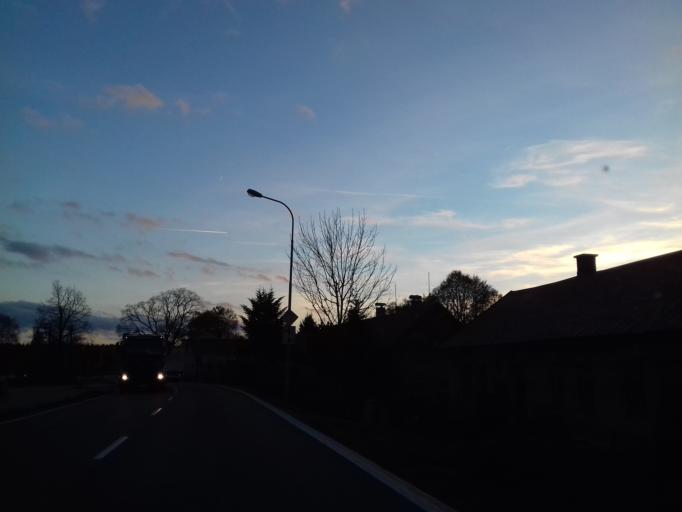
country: CZ
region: Vysocina
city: Krizova
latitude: 49.6924
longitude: 15.7972
